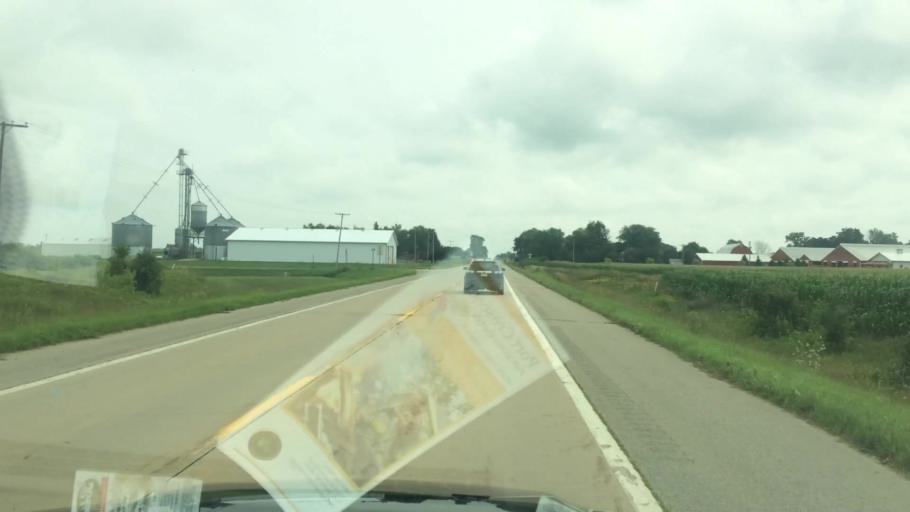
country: US
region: Michigan
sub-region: Huron County
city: Bad Axe
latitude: 44.0423
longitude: -82.9513
